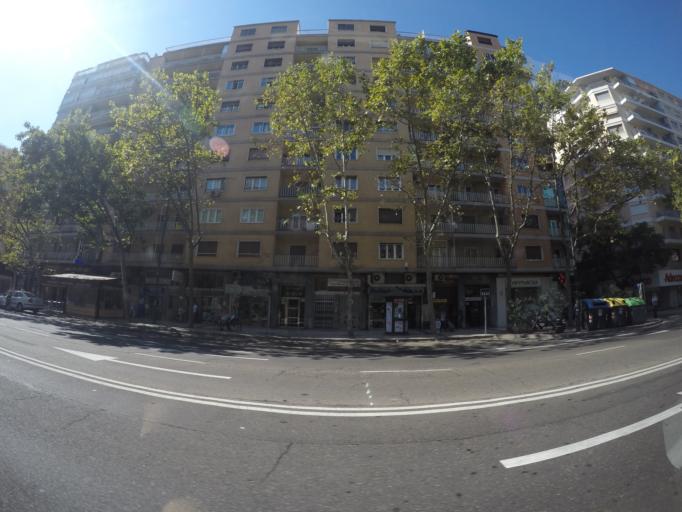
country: ES
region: Aragon
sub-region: Provincia de Zaragoza
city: Zaragoza
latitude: 41.6506
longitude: -0.8891
